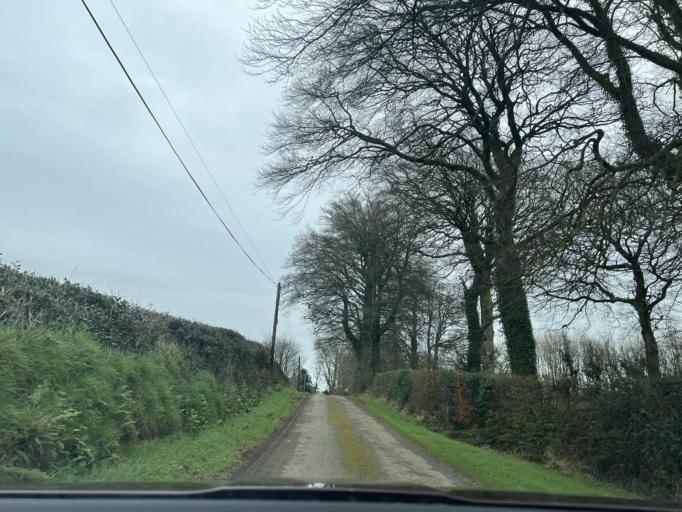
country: IE
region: Leinster
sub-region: Loch Garman
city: Castlebridge
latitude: 52.3881
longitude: -6.5439
